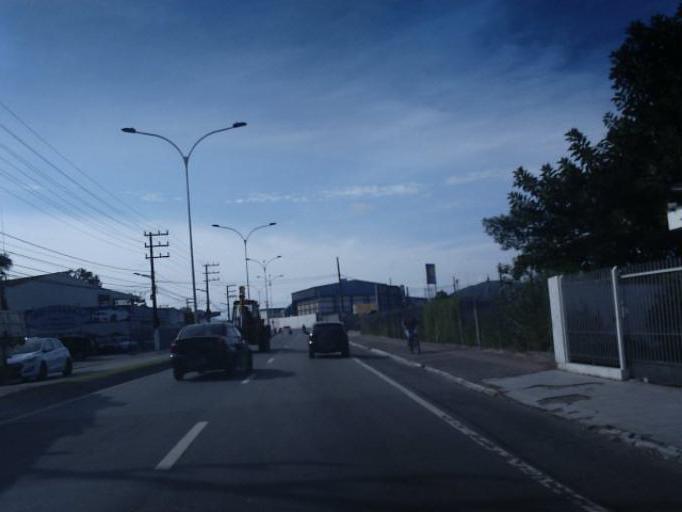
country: BR
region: Santa Catarina
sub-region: Itajai
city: Itajai
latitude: -26.8855
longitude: -48.6910
